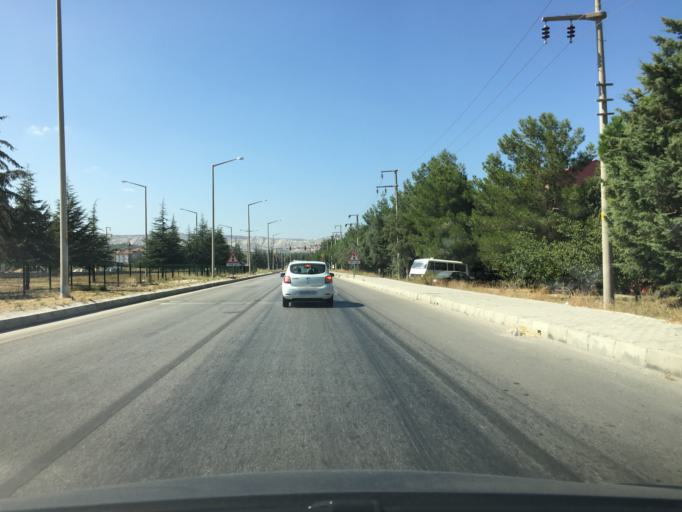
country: TR
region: Burdur
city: Burdur
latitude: 37.7311
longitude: 30.3068
